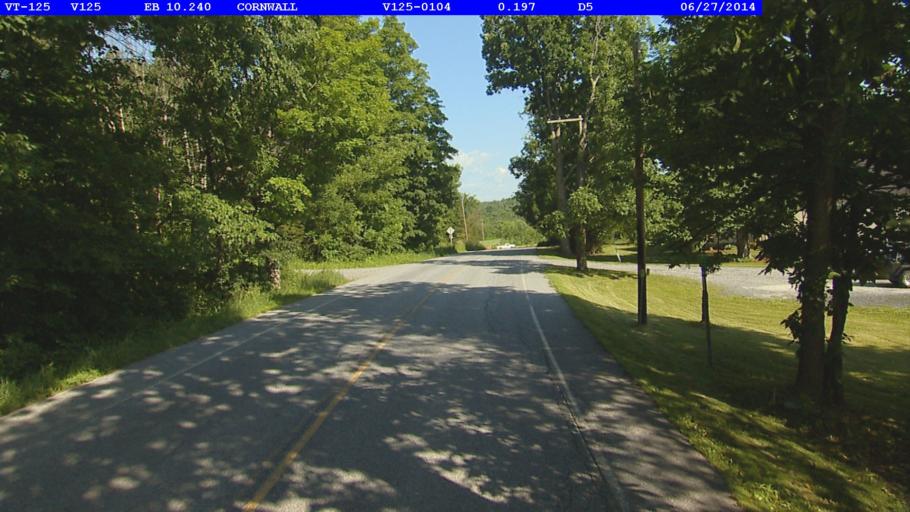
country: US
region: Vermont
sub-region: Addison County
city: Middlebury (village)
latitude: 43.9950
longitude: -73.2540
